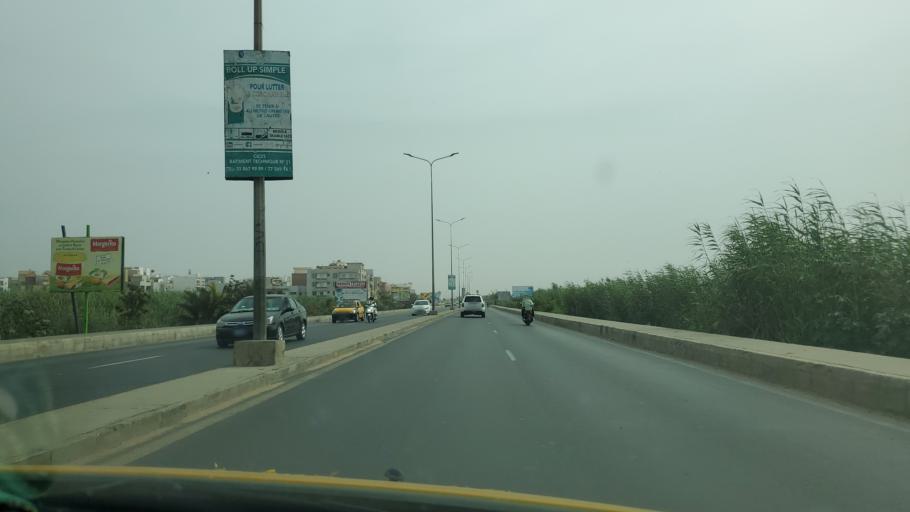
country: SN
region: Dakar
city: Pikine
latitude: 14.7577
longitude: -17.4034
